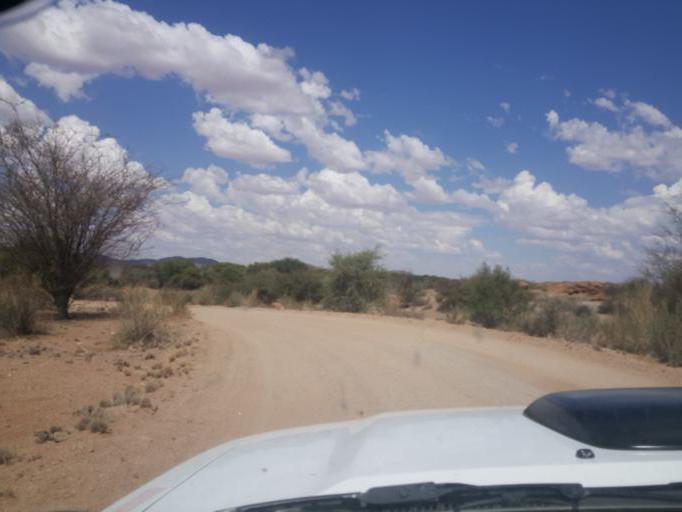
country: ZA
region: Northern Cape
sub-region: Siyanda District Municipality
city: Kakamas
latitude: -28.6034
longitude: 20.3227
